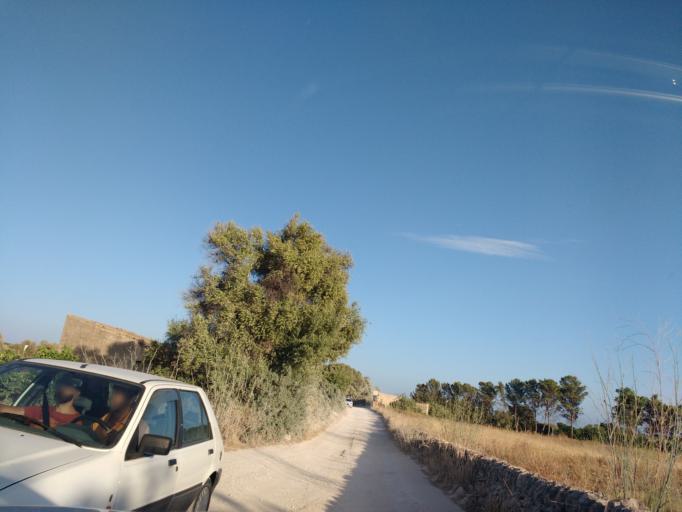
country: IT
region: Sicily
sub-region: Provincia di Siracusa
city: Noto
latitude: 36.8193
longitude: 15.0968
